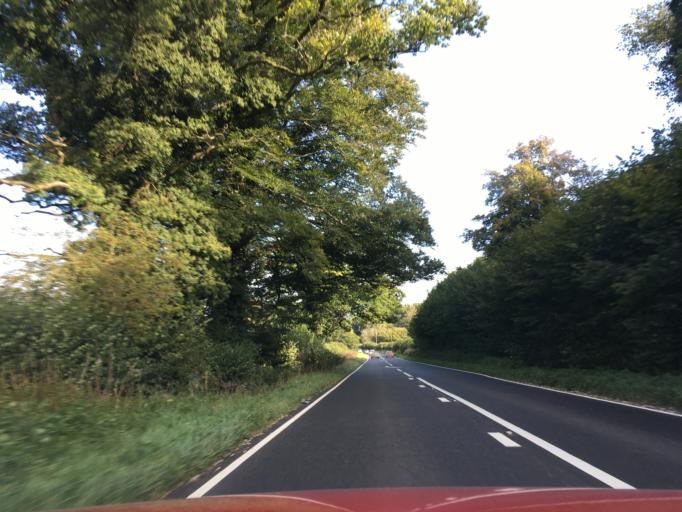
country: GB
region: England
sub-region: Hampshire
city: Four Marks
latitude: 51.1681
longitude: -1.0379
